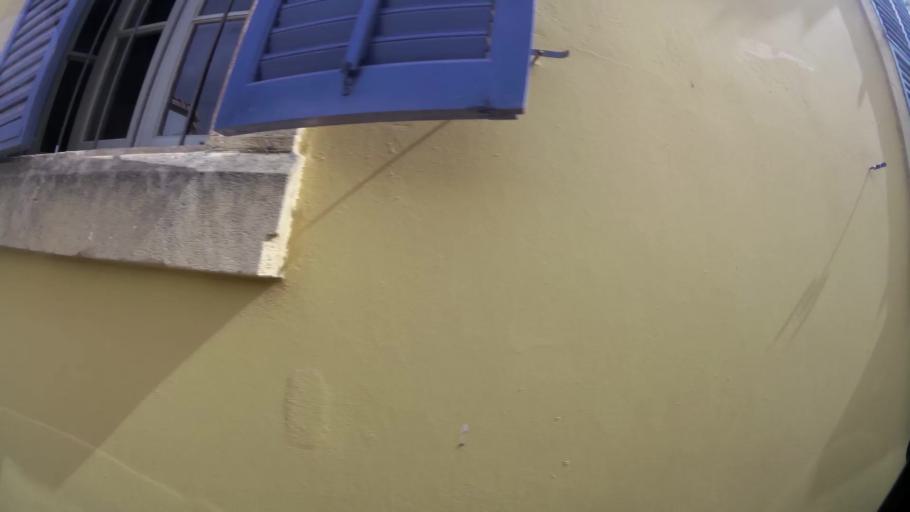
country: CY
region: Lefkosia
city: Nicosia
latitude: 35.1759
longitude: 33.3699
